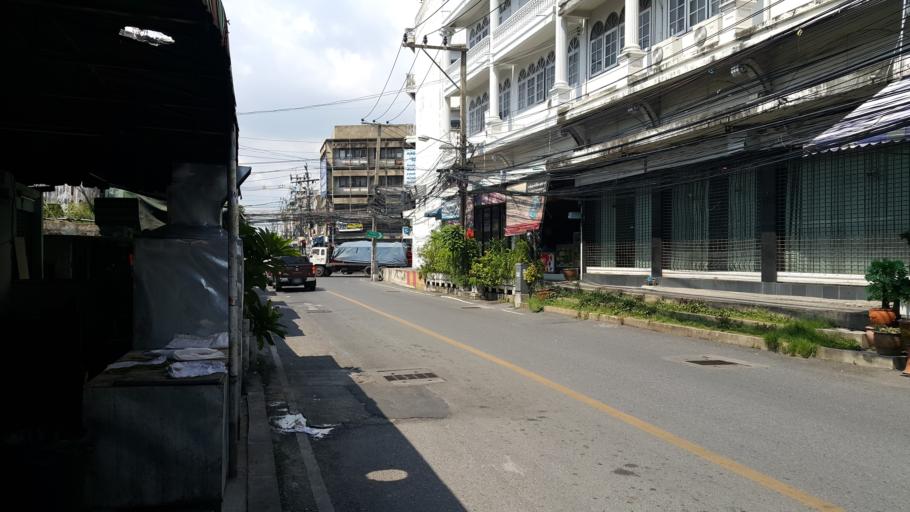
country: TH
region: Bangkok
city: Phra Khanong
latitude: 13.7107
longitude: 100.6100
